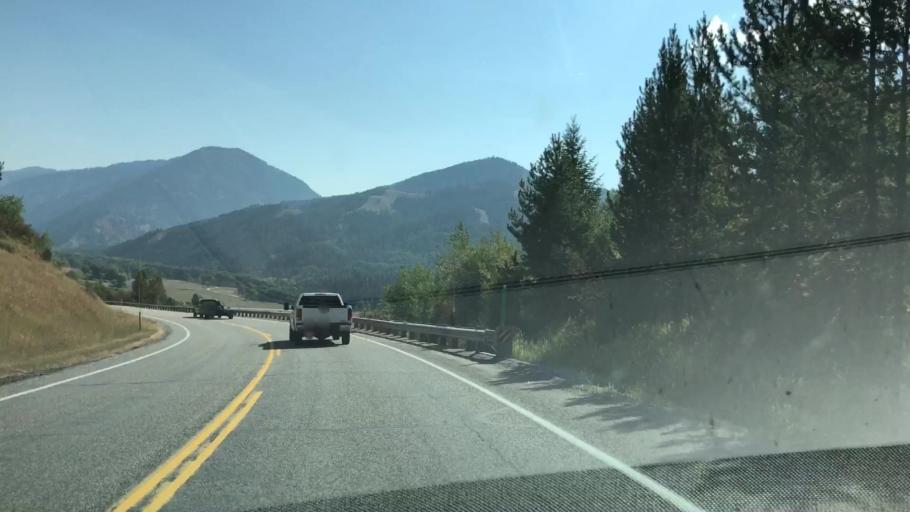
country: US
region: Wyoming
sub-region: Teton County
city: Hoback
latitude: 43.2505
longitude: -111.1147
